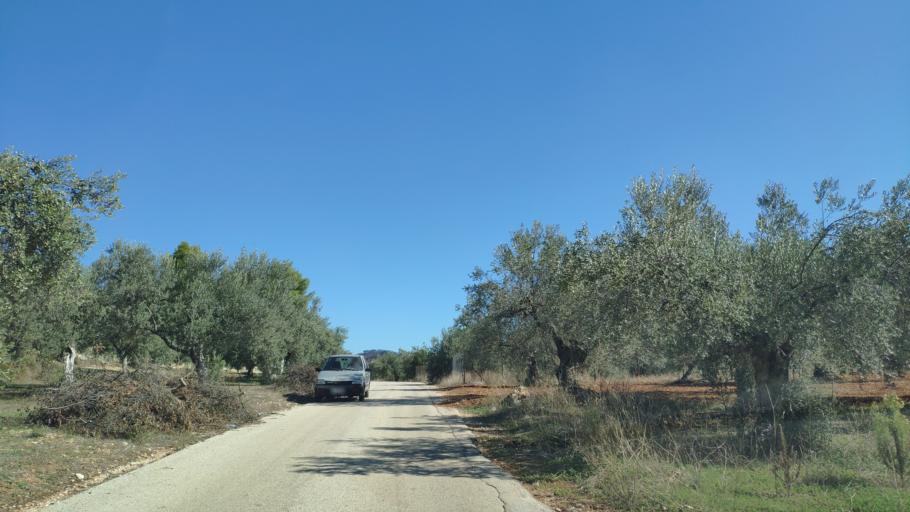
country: GR
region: Peloponnese
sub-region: Nomos Korinthias
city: Athikia
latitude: 37.8410
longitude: 22.9216
